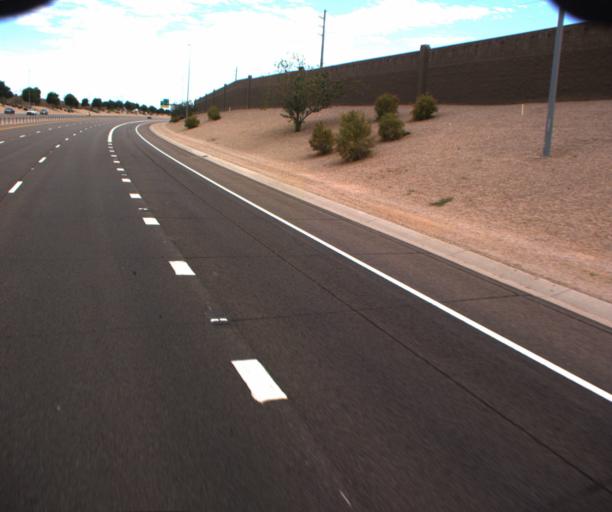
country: US
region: Arizona
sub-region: Maricopa County
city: Gilbert
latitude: 33.3270
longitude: -111.7308
